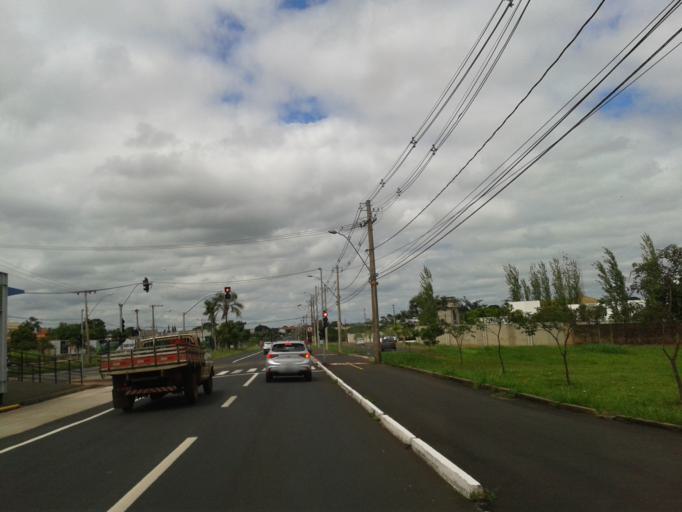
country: BR
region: Minas Gerais
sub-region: Uberaba
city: Uberaba
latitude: -19.7461
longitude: -47.9659
